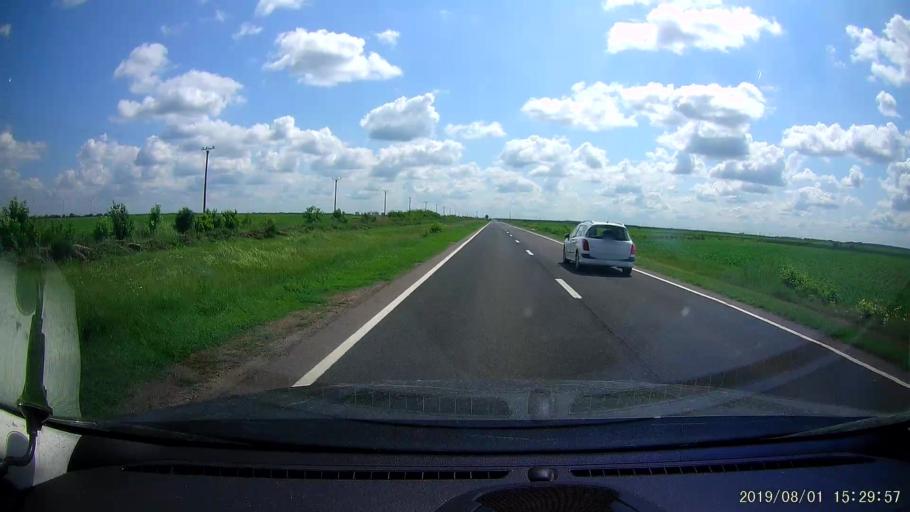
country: RO
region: Braila
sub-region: Comuna Viziru
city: Viziru
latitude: 44.9724
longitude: 27.6870
